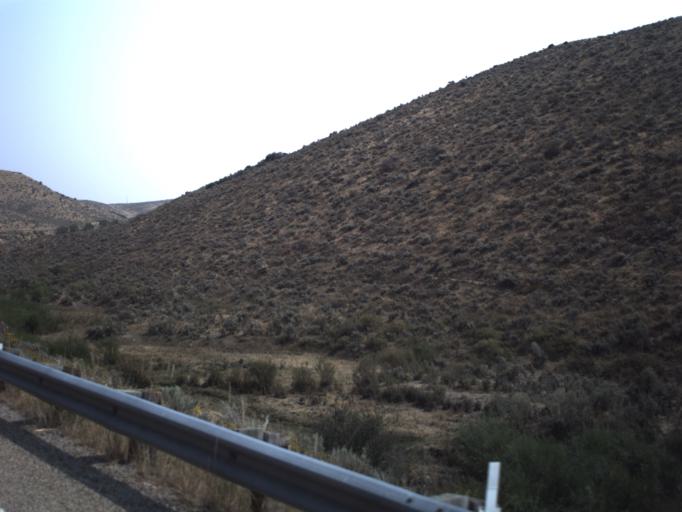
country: US
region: Utah
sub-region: Morgan County
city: Morgan
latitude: 40.9320
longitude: -111.5690
